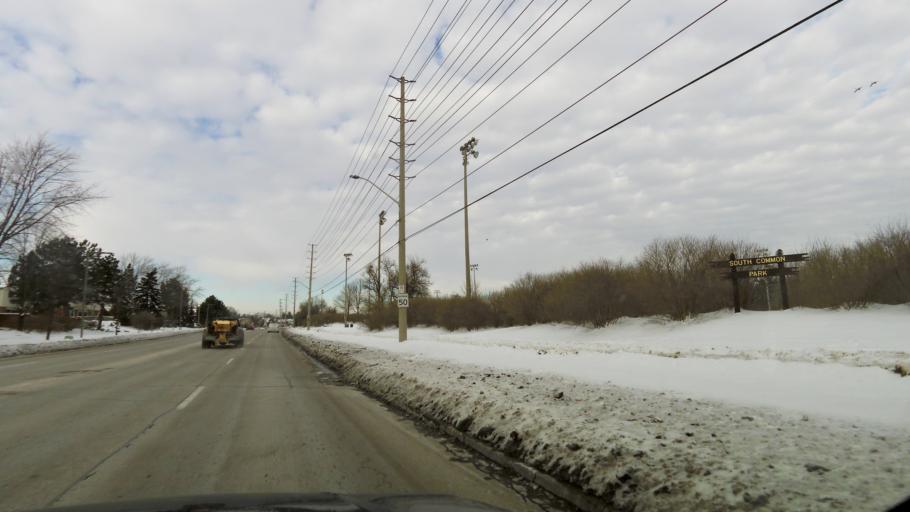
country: CA
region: Ontario
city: Mississauga
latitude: 43.5394
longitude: -79.6890
